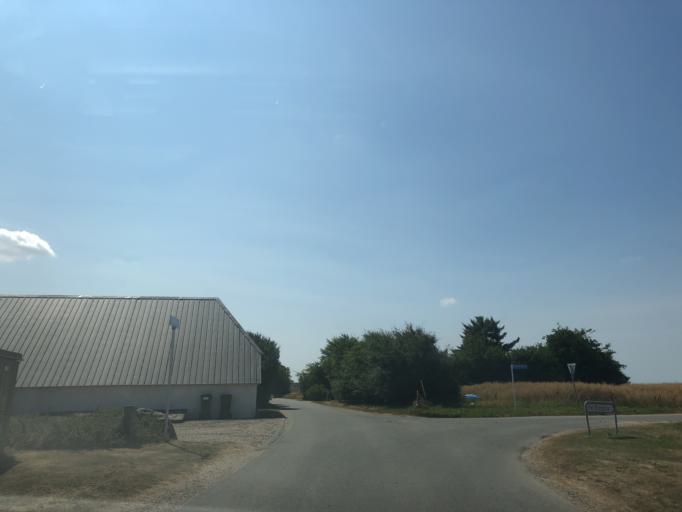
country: DK
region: North Denmark
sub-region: Morso Kommune
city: Nykobing Mors
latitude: 56.8210
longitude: 8.9912
